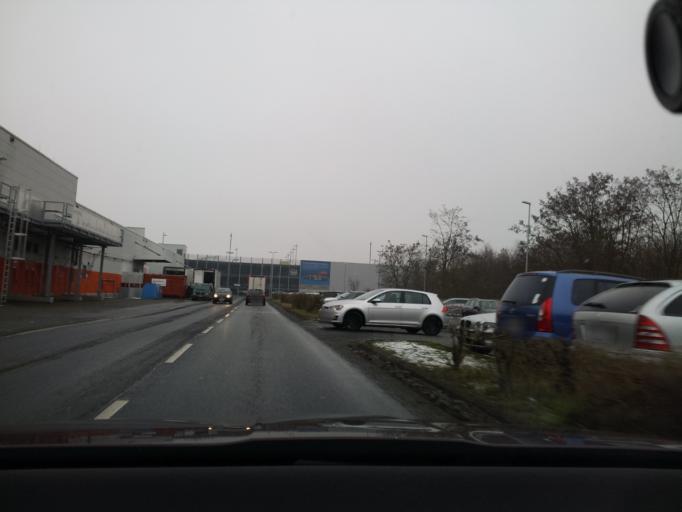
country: DE
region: Brandenburg
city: Wildau
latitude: 52.3152
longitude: 13.6114
